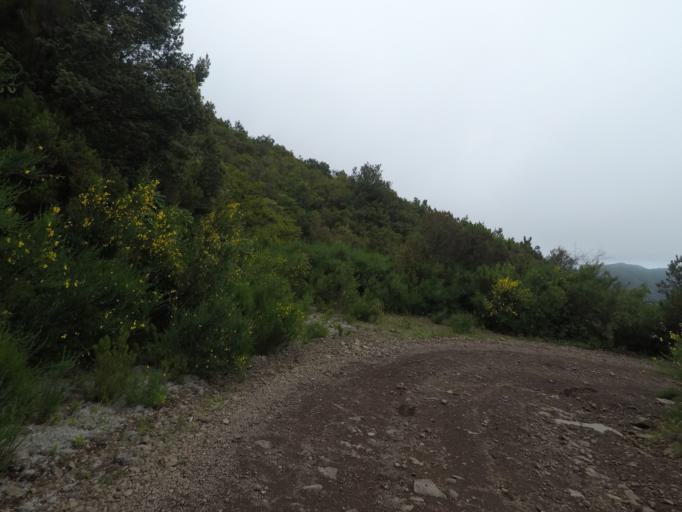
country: PT
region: Madeira
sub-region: Sao Vicente
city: Sao Vicente
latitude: 32.7726
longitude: -17.0575
